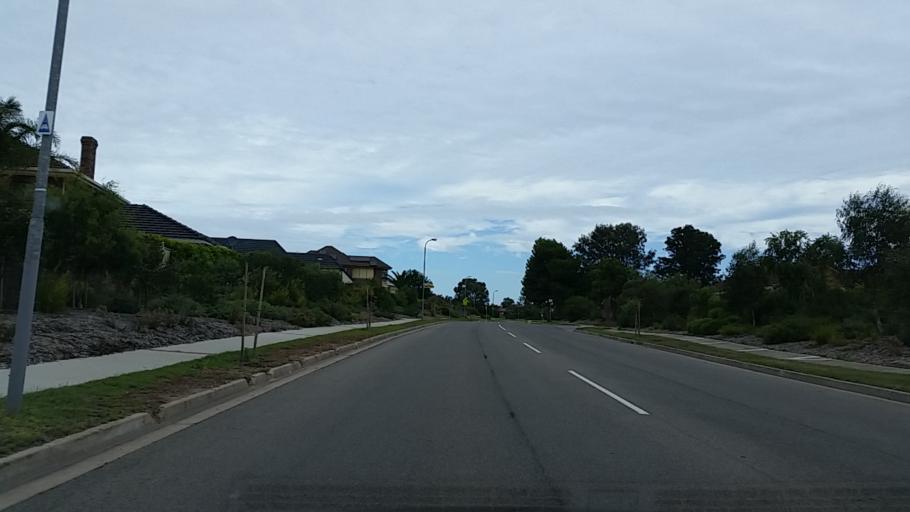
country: AU
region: South Australia
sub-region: Charles Sturt
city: West Lakes Shore
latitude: -34.8642
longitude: 138.4918
